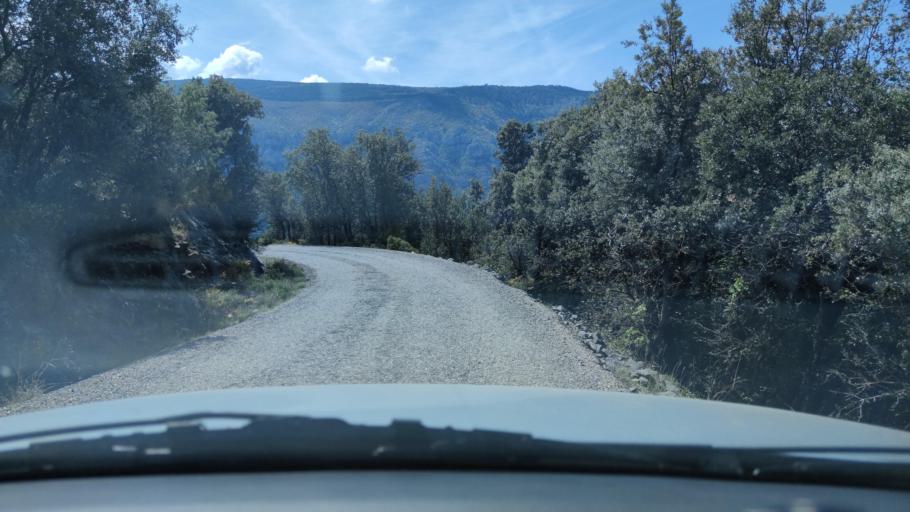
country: ES
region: Catalonia
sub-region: Provincia de Lleida
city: Sort
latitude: 42.3184
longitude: 1.0900
